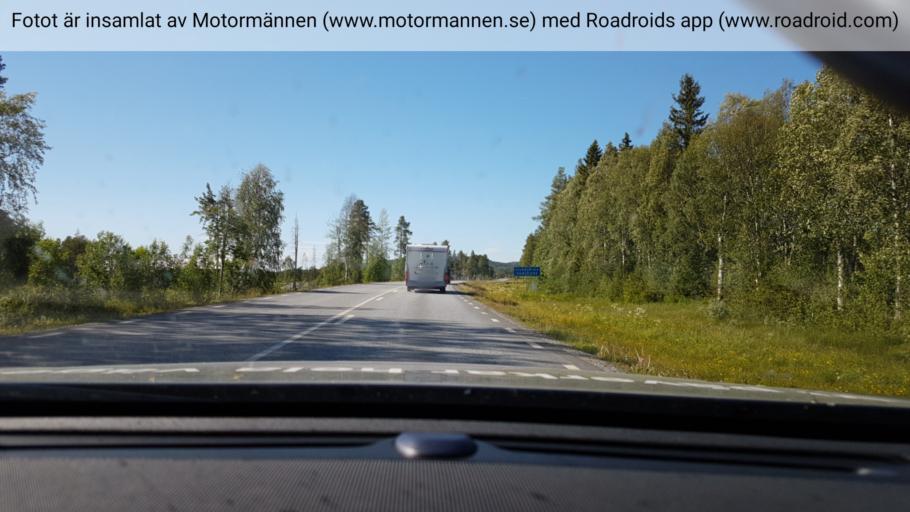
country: SE
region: Vaesterbotten
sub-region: Vilhelmina Kommun
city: Vilhelmina
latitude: 64.5849
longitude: 16.7391
